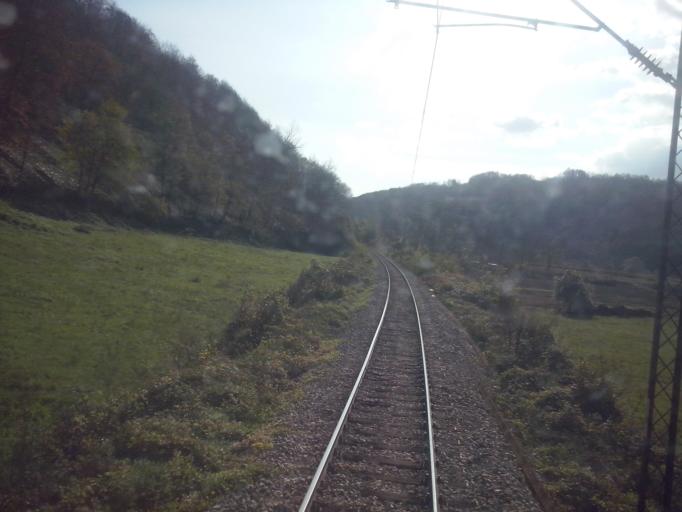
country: RS
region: Central Serbia
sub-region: Zlatiborski Okrug
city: Pozega
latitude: 43.9187
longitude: 19.9914
